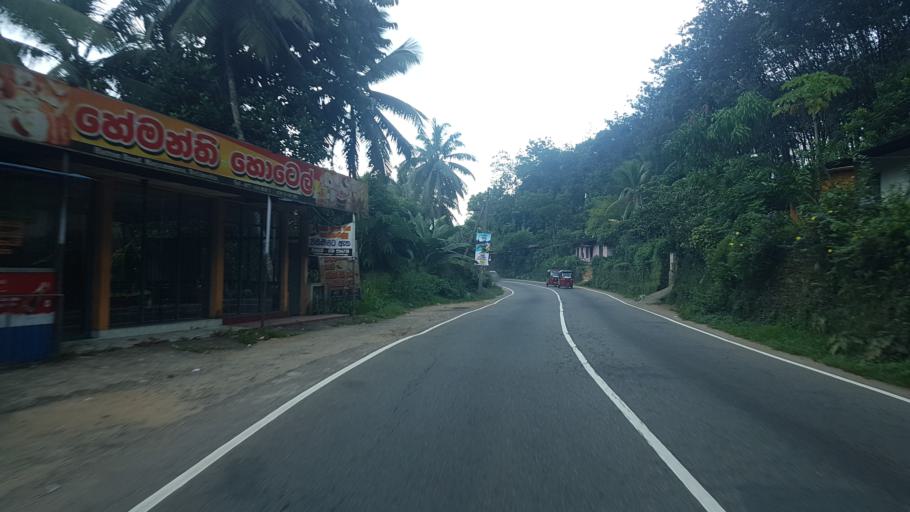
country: LK
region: Western
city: Hanwella Ihala
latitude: 7.0034
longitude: 80.2625
